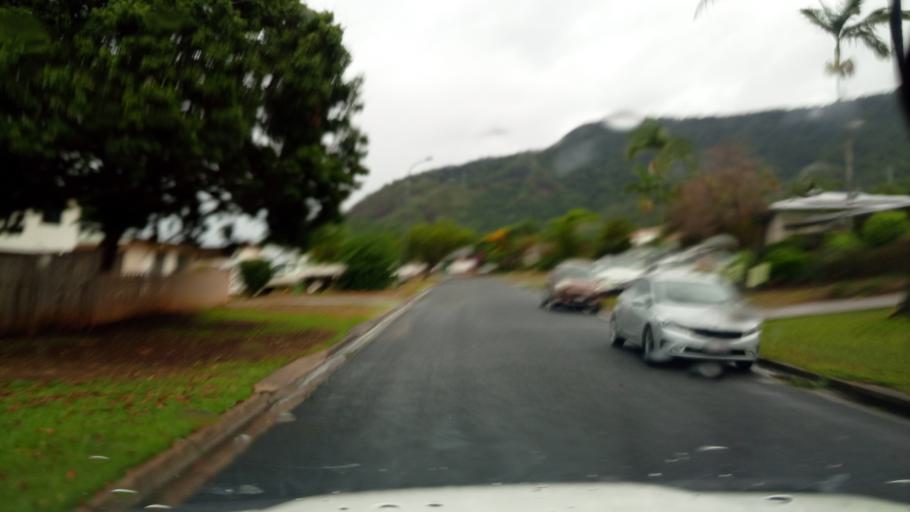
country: AU
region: Queensland
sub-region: Cairns
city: Woree
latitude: -16.9566
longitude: 145.7295
